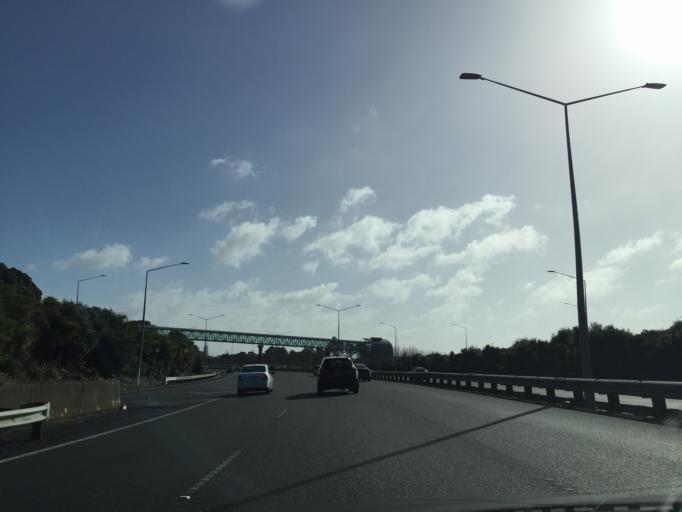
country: NZ
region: Auckland
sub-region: Auckland
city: North Shore
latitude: -36.7995
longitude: 174.7613
